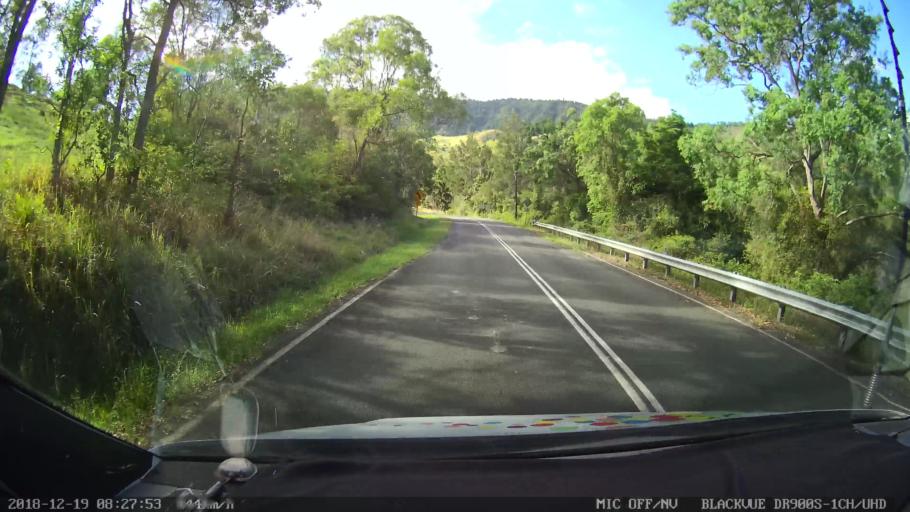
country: AU
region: New South Wales
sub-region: Kyogle
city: Kyogle
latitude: -28.3198
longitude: 152.9291
